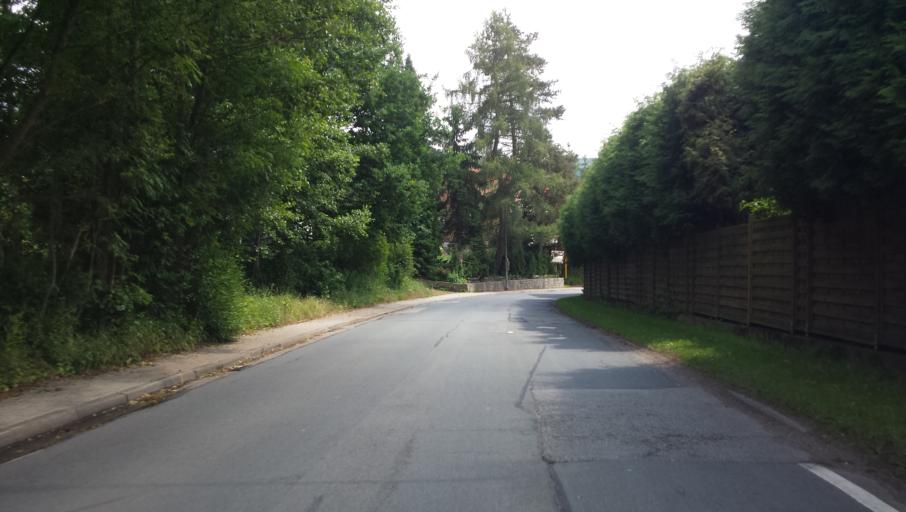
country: DE
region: Hesse
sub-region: Regierungsbezirk Darmstadt
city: Furth
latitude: 49.6527
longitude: 8.7756
